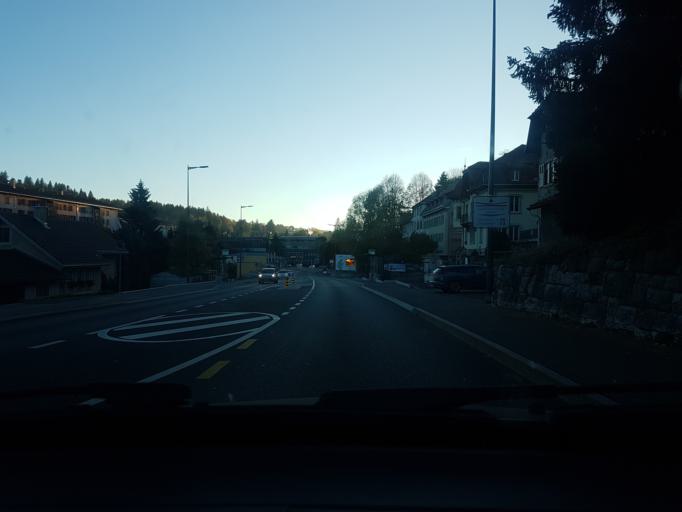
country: CH
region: Neuchatel
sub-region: Le Locle District
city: Le Locle
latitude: 47.0657
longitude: 6.7626
